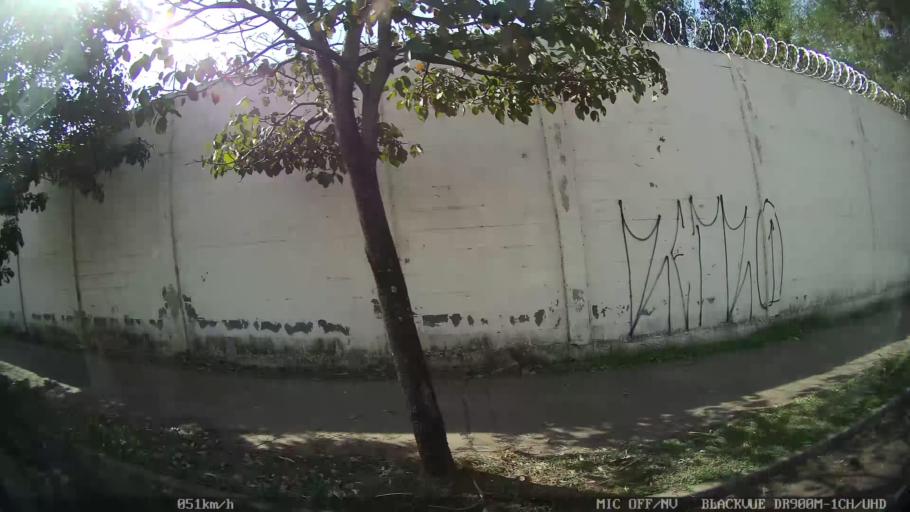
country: BR
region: Sao Paulo
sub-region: Piracicaba
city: Piracicaba
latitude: -22.7015
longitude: -47.6757
